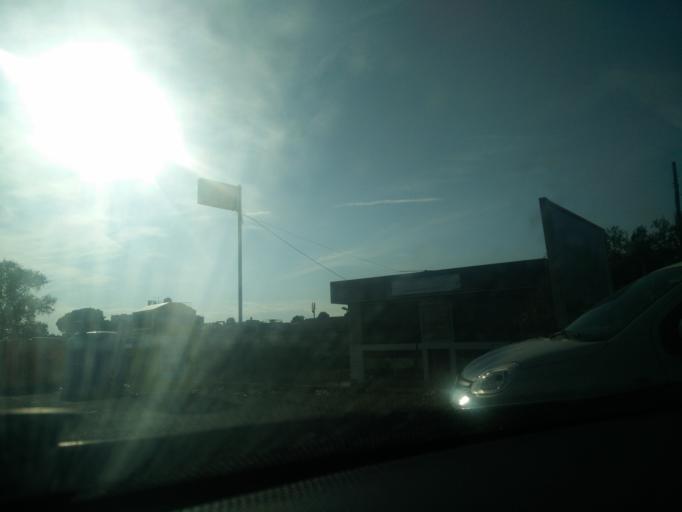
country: IT
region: Tuscany
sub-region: Provincia di Massa-Carrara
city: Massa
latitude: 44.0223
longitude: 10.1199
